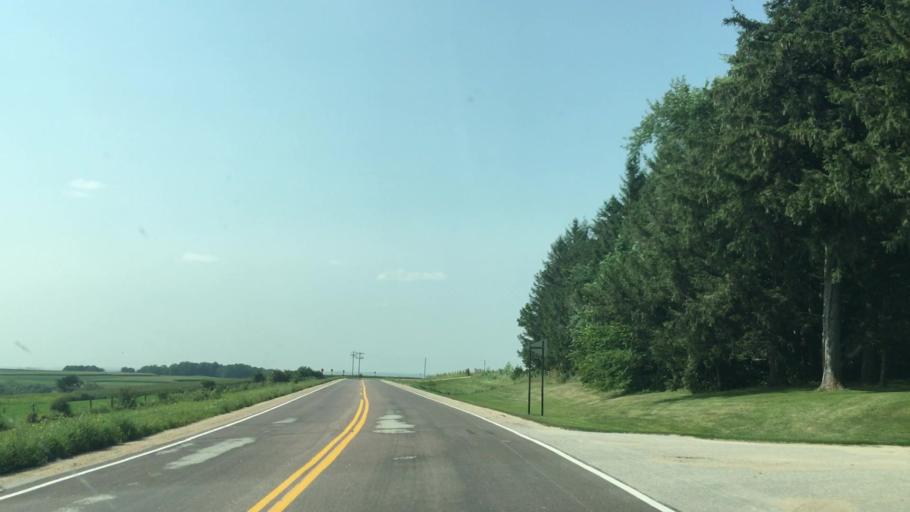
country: US
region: Minnesota
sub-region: Fillmore County
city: Harmony
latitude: 43.6493
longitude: -91.9275
